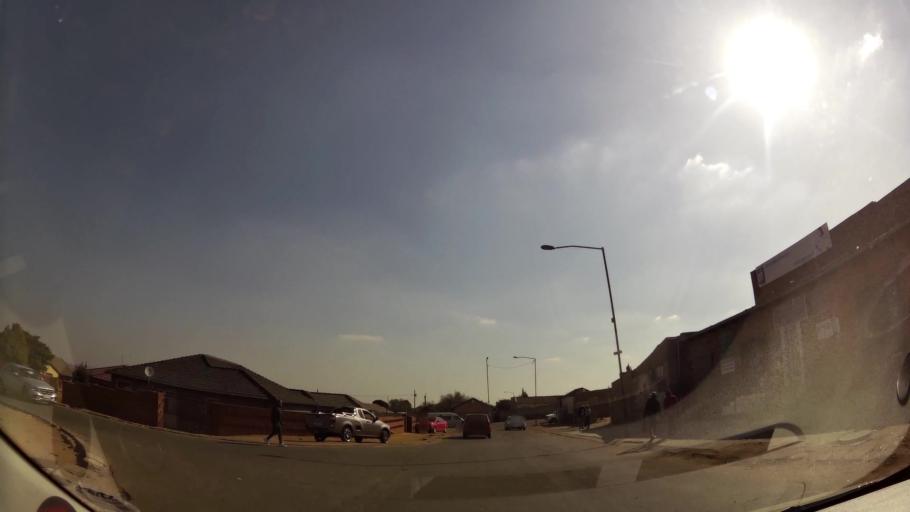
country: ZA
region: Gauteng
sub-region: City of Johannesburg Metropolitan Municipality
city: Roodepoort
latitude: -26.1674
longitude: 27.7939
